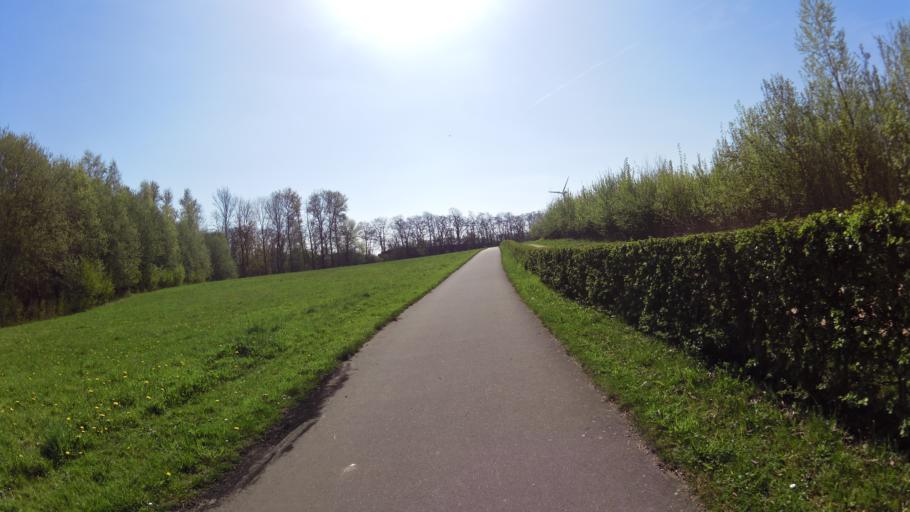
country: DE
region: North Rhine-Westphalia
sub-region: Regierungsbezirk Koln
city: Alsdorf
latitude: 50.9058
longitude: 6.1539
